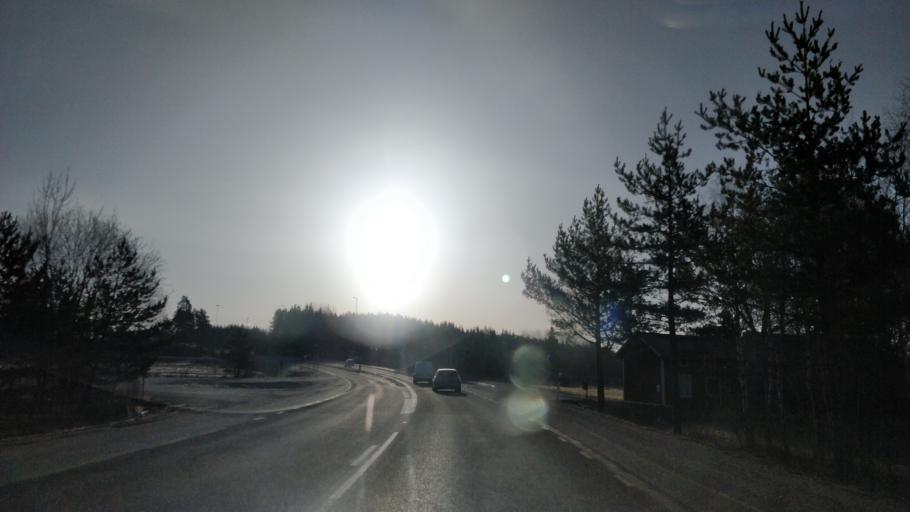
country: SE
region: Uppsala
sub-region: Enkopings Kommun
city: Enkoping
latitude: 59.6460
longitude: 17.1374
